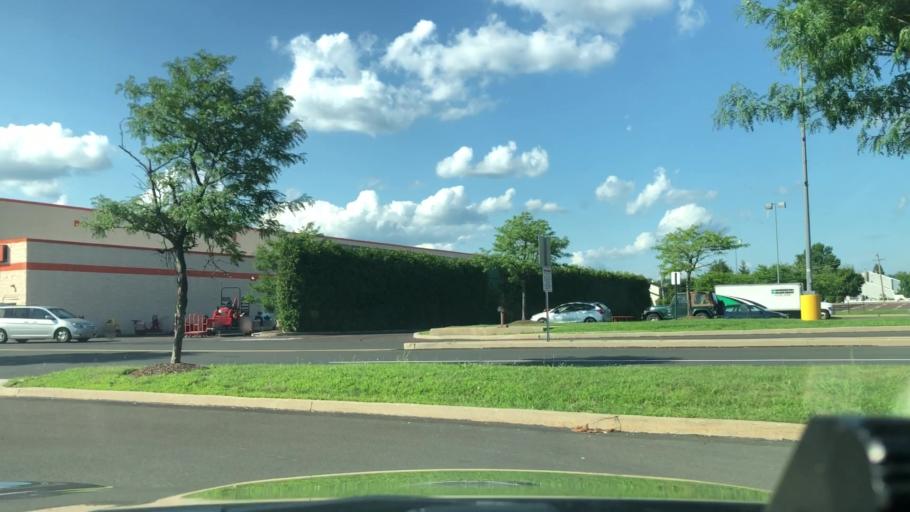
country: US
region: Pennsylvania
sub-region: Montgomery County
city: Montgomeryville
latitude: 40.2465
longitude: -75.2385
